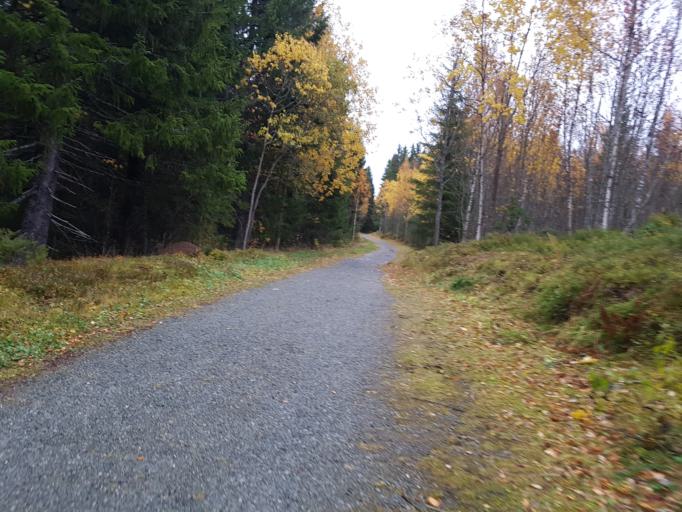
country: NO
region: Sor-Trondelag
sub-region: Trondheim
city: Trondheim
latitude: 63.3808
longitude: 10.3258
